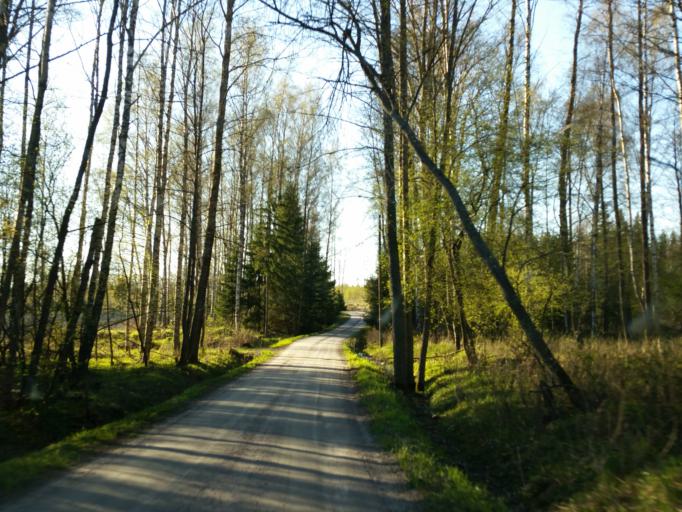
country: FI
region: Uusimaa
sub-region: Helsinki
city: Espoo
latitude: 60.1143
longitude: 24.6230
